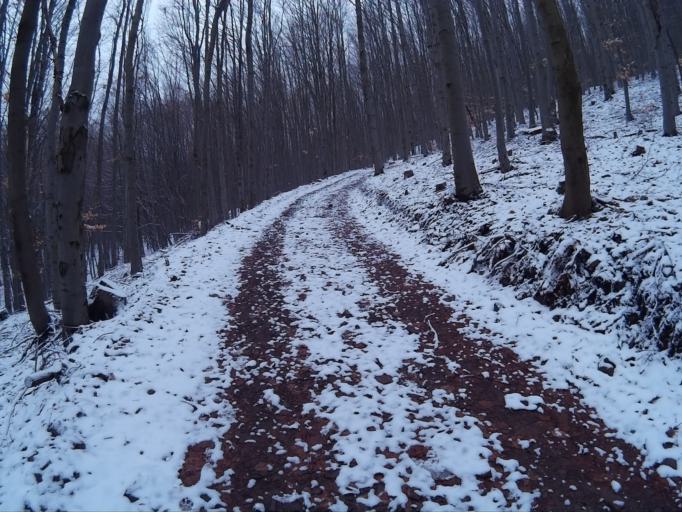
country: HU
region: Borsod-Abauj-Zemplen
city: Gonc
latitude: 48.5755
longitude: 21.4396
